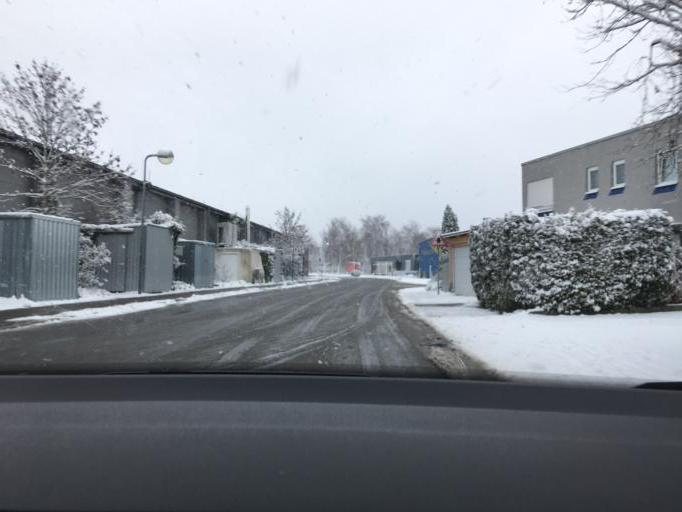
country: DE
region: Baden-Wuerttemberg
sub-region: Freiburg Region
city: Gottmadingen
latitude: 47.7357
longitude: 8.7877
